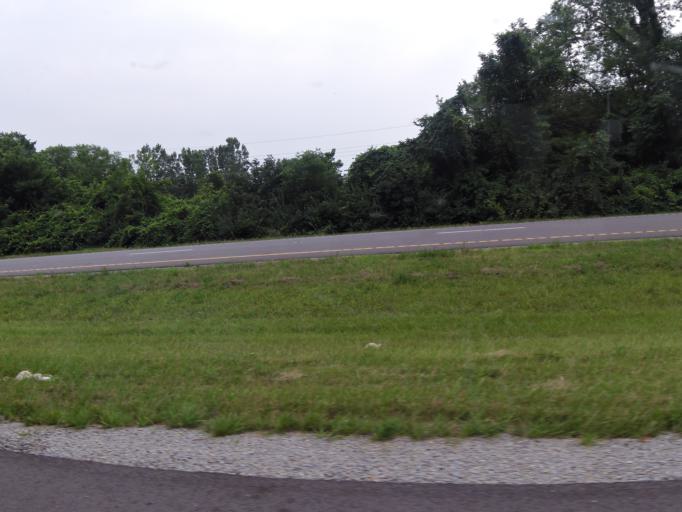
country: US
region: Ohio
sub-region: Warren County
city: Waynesville
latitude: 39.5357
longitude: -84.0761
